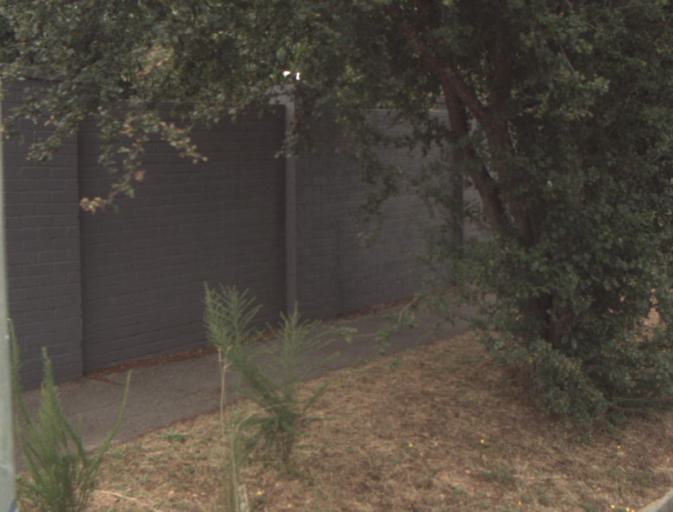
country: AU
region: Tasmania
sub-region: Launceston
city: Launceston
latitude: -41.4386
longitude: 147.1171
